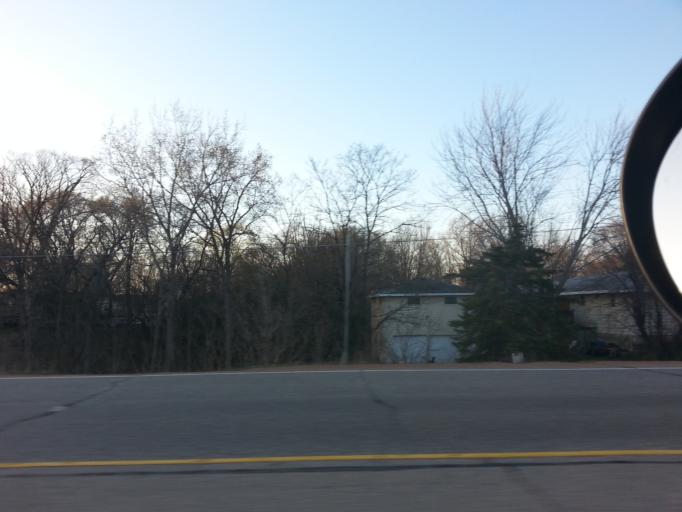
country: US
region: Minnesota
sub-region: Scott County
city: Prior Lake
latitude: 44.7063
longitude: -93.4324
